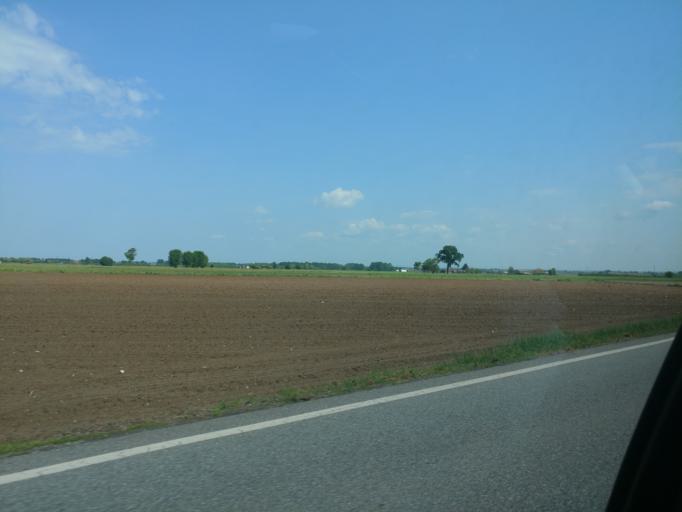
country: IT
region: Piedmont
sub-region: Provincia di Torino
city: Cavour
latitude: 44.7680
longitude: 7.3934
